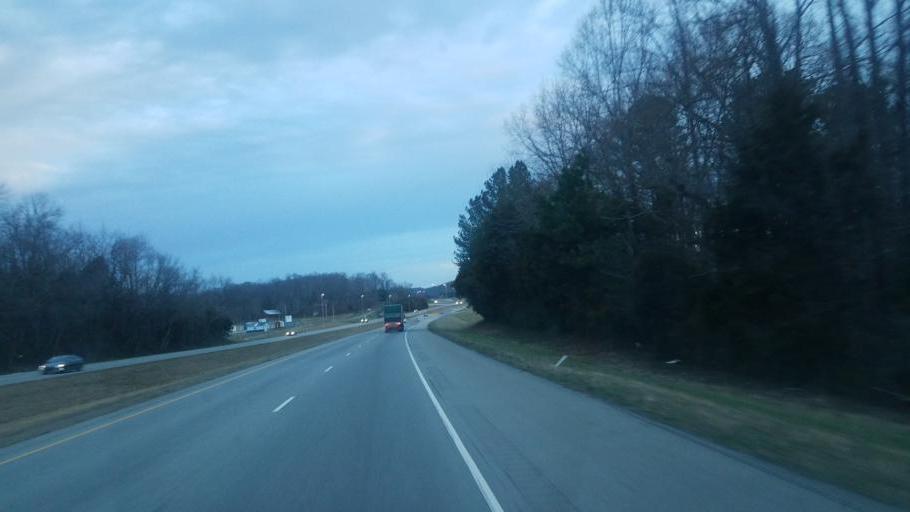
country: US
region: Tennessee
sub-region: White County
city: Sparta
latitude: 35.9550
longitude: -85.4852
